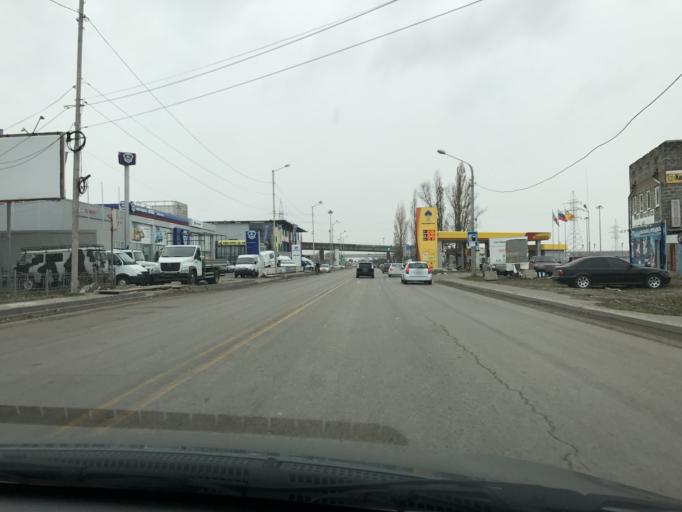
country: RU
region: Rostov
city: Rostov-na-Donu
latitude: 47.2064
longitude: 39.7260
